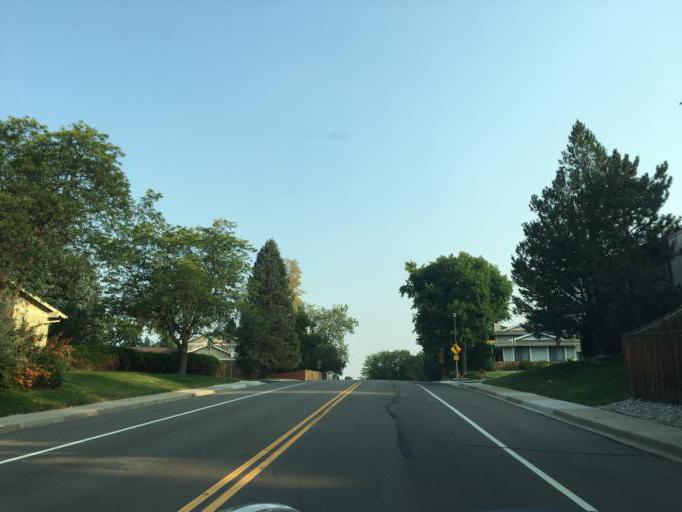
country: US
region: Colorado
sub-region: Adams County
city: Westminster
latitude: 39.8821
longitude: -105.0478
